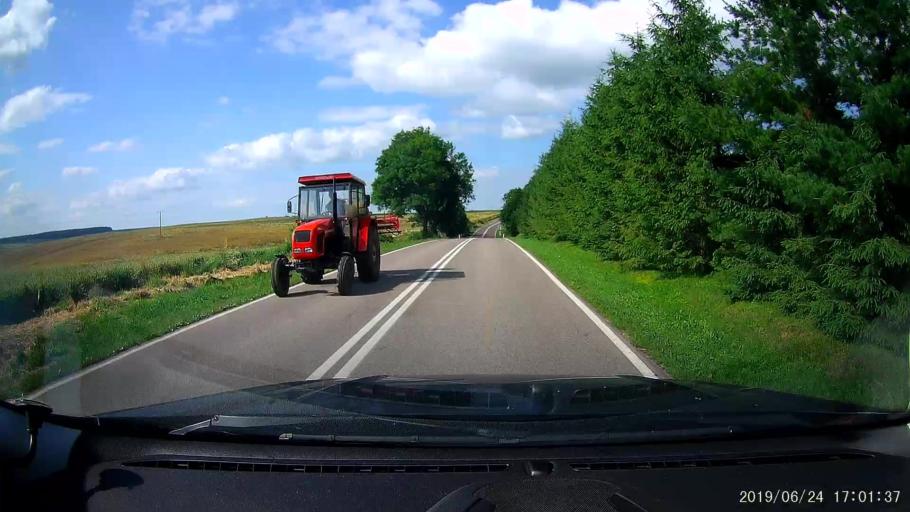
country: PL
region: Lublin Voivodeship
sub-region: Powiat tomaszowski
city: Telatyn
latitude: 50.5413
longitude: 23.9236
